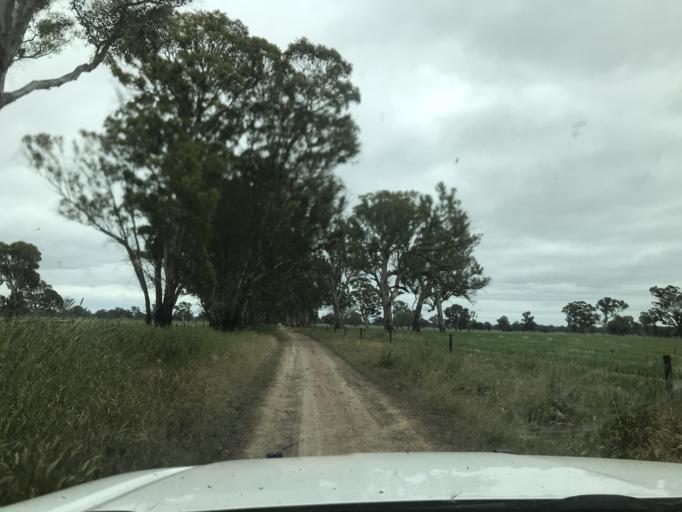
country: AU
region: South Australia
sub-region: Wattle Range
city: Penola
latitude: -37.1787
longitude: 141.0556
